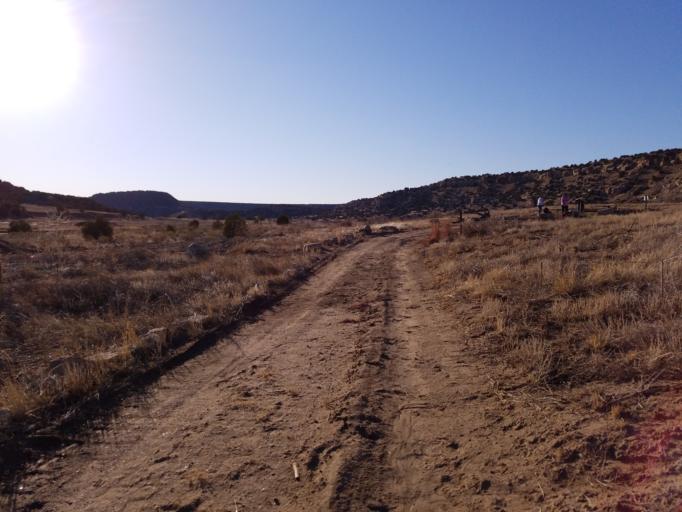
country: US
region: Colorado
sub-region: Otero County
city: La Junta
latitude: 37.6179
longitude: -103.5971
